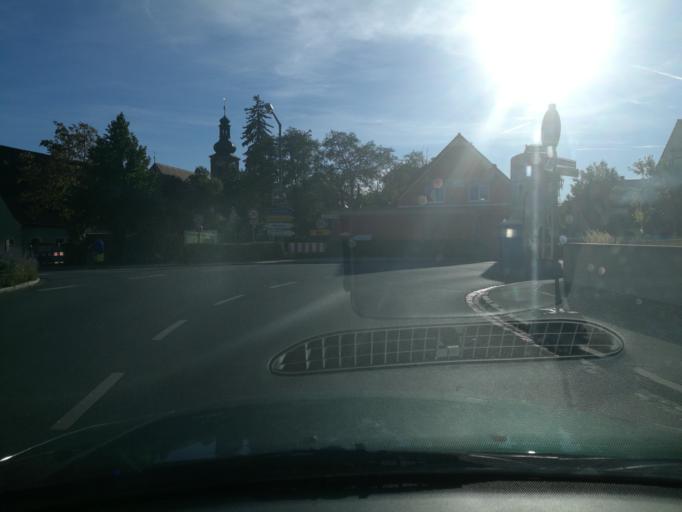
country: DE
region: Bavaria
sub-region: Regierungsbezirk Mittelfranken
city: Erlangen
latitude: 49.5688
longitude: 10.9619
